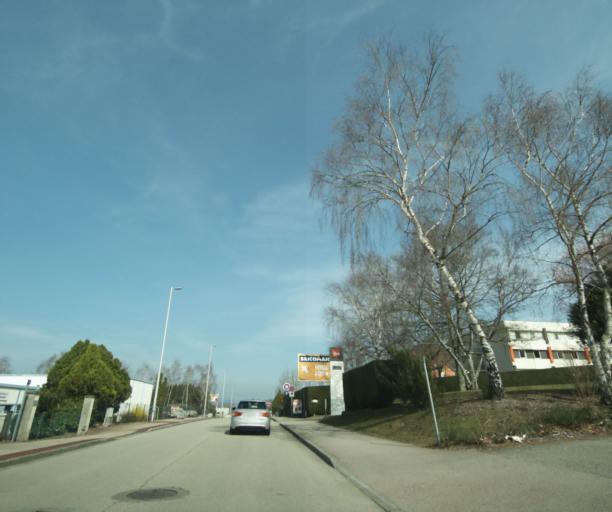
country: FR
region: Limousin
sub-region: Departement de la Haute-Vienne
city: Rilhac-Rancon
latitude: 45.8856
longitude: 1.2902
